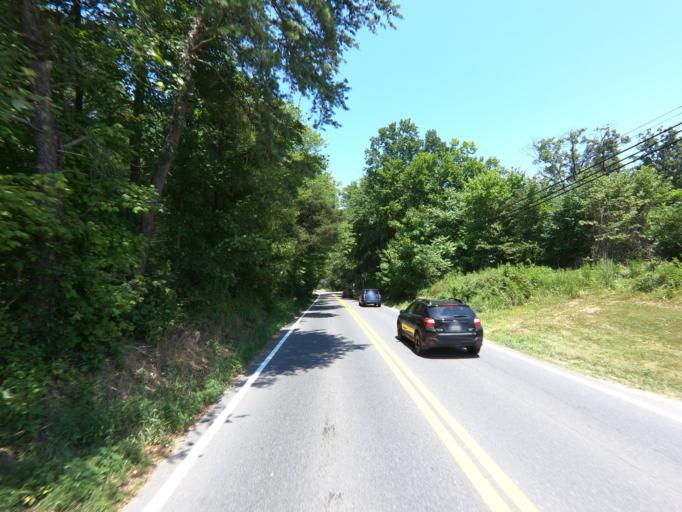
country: US
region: Maryland
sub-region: Montgomery County
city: Clarksburg
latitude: 39.2598
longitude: -77.3027
